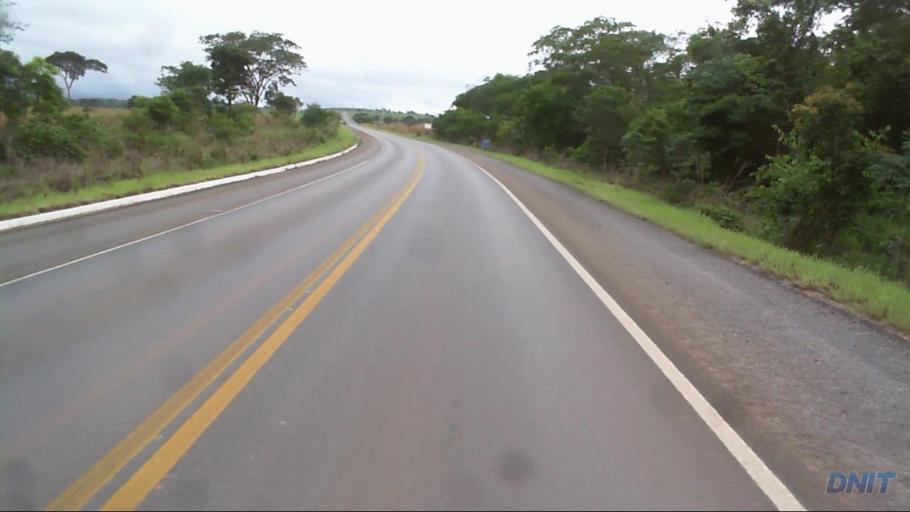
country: BR
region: Goias
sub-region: Padre Bernardo
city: Padre Bernardo
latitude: -15.2209
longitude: -48.5475
